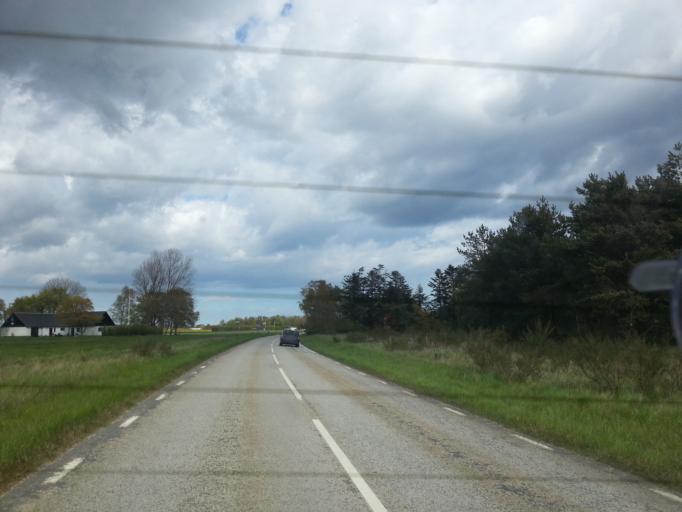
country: SE
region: Skane
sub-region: Simrishamns Kommun
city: Simrishamn
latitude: 55.4104
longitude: 14.1936
